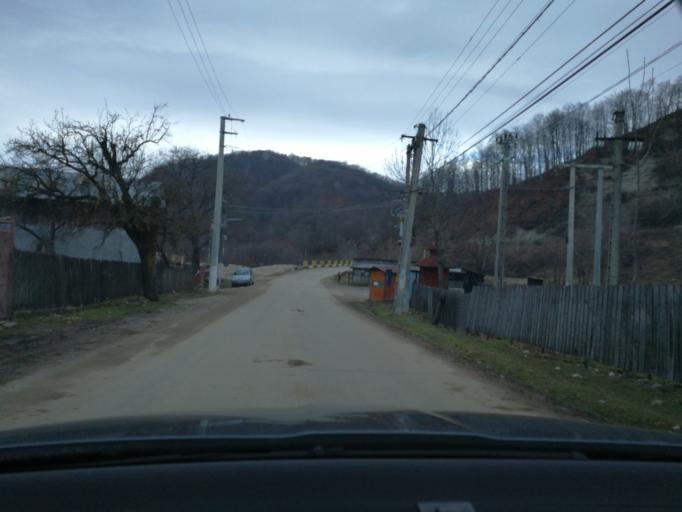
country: RO
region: Dambovita
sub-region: Comuna Bezdead
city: Bezdead
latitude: 45.1667
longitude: 25.5357
